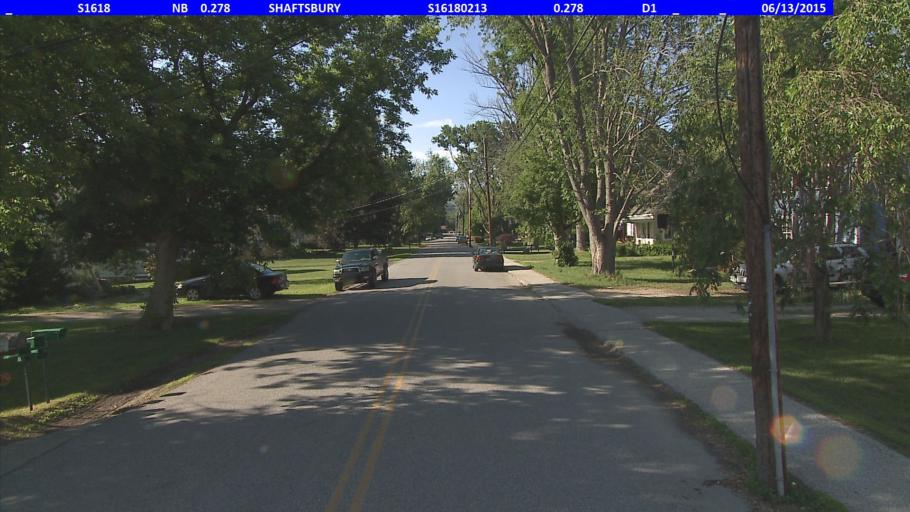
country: US
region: Vermont
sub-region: Bennington County
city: North Bennington
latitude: 42.9434
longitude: -73.2127
